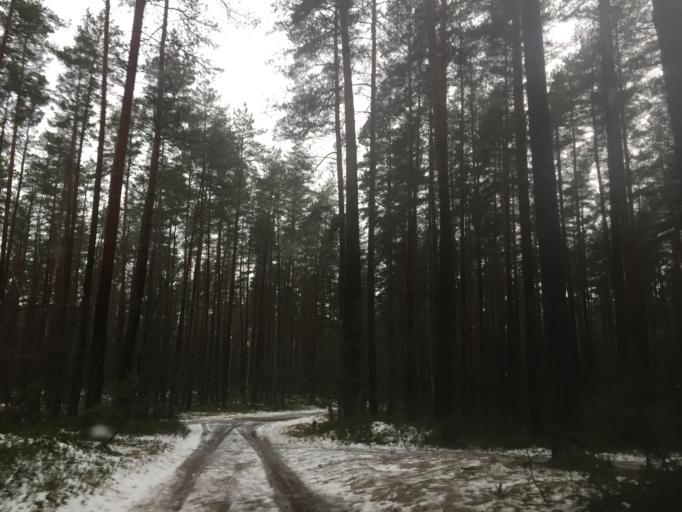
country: LV
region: Stopini
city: Ulbroka
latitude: 56.9512
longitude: 24.3428
